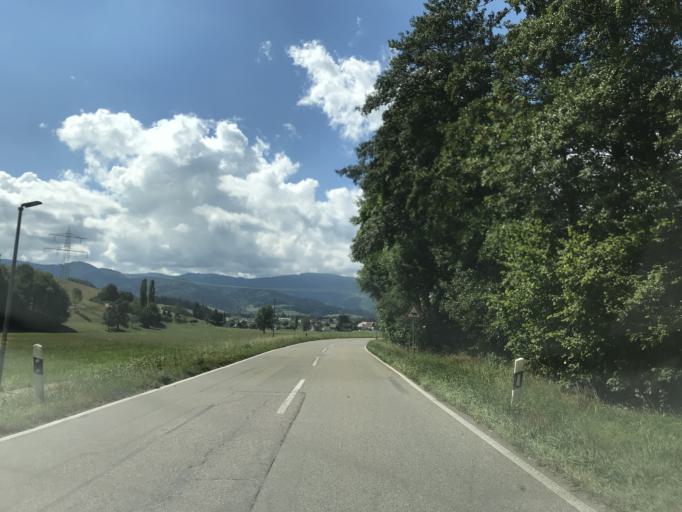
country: DE
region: Baden-Wuerttemberg
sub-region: Freiburg Region
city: Stegen
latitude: 47.9922
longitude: 7.9740
